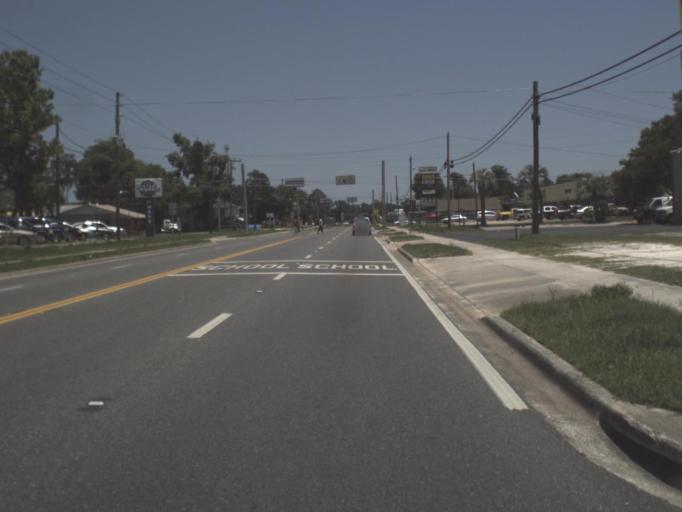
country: US
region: Florida
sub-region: Columbia County
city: Watertown
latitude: 30.1878
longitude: -82.6107
